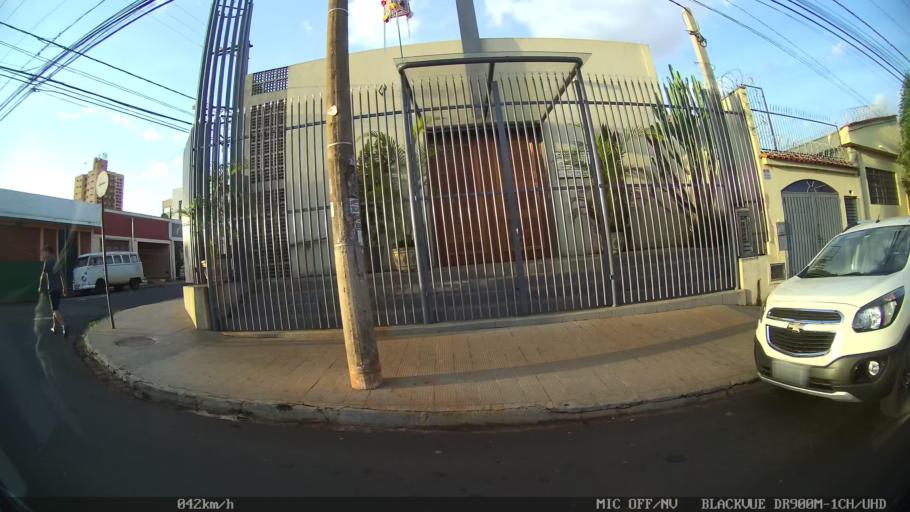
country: BR
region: Sao Paulo
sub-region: Ribeirao Preto
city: Ribeirao Preto
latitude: -21.1600
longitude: -47.8343
